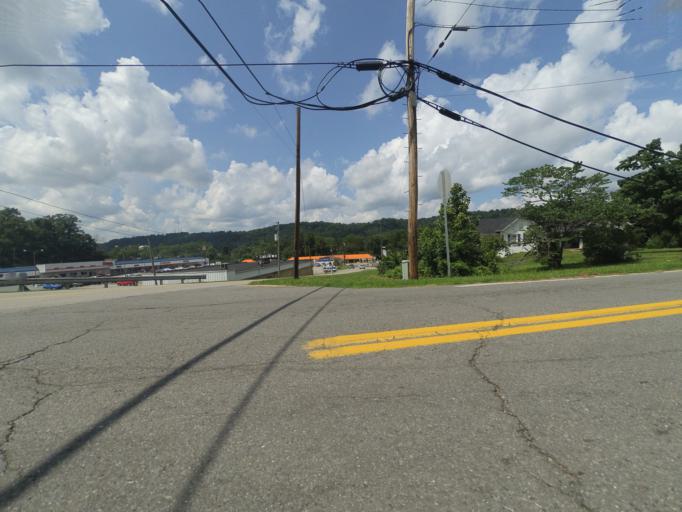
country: US
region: West Virginia
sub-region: Cabell County
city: Pea Ridge
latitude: 38.4102
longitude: -82.3644
